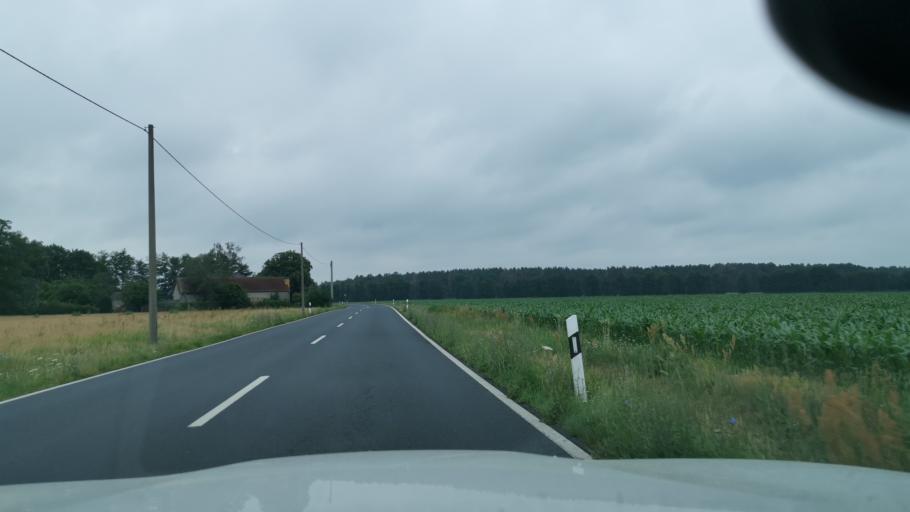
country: DE
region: Saxony-Anhalt
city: Jessen
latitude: 51.8404
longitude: 13.0206
